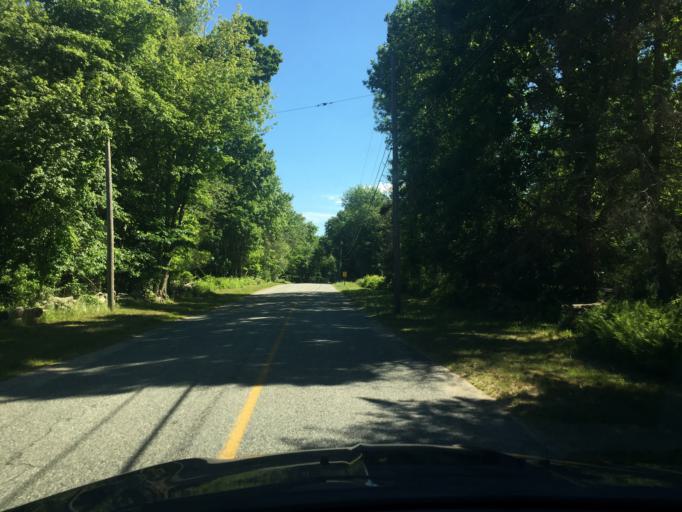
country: US
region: Rhode Island
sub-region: Washington County
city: Hopkinton
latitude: 41.4890
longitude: -71.8096
